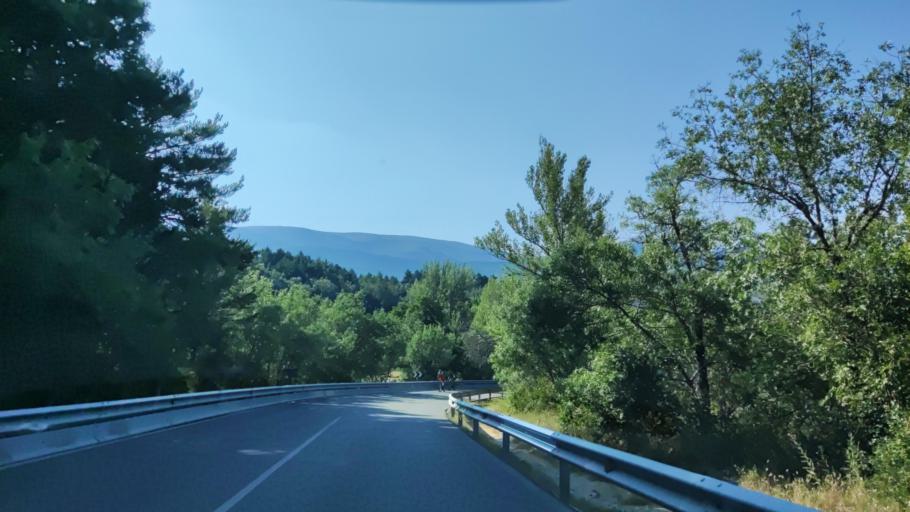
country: ES
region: Madrid
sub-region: Provincia de Madrid
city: Rascafria
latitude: 40.8822
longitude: -3.8861
